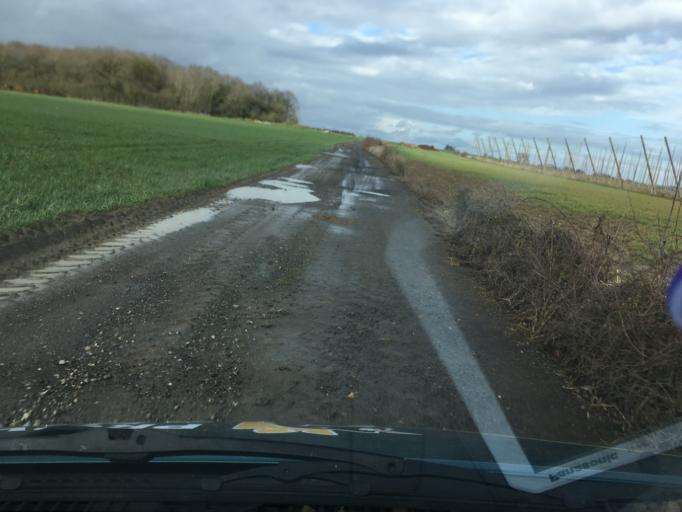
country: BE
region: Wallonia
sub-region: Province de Namur
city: Doische
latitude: 50.1665
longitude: 4.7533
